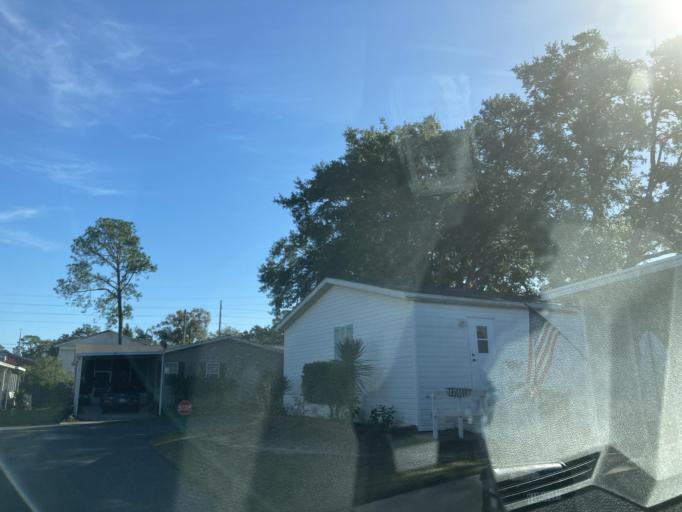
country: US
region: Mississippi
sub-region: Harrison County
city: D'Iberville
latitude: 30.4053
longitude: -88.9404
